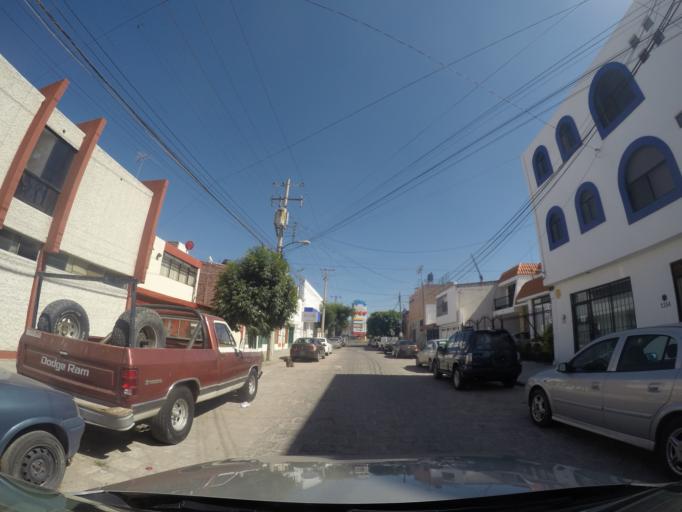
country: MX
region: San Luis Potosi
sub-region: San Luis Potosi
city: San Luis Potosi
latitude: 22.1493
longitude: -101.0142
